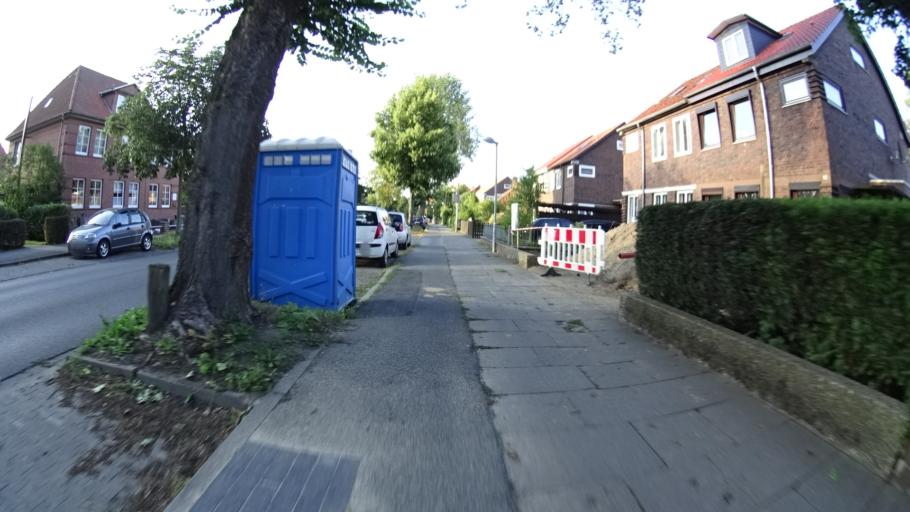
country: DE
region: Lower Saxony
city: Lueneburg
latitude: 53.2379
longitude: 10.3993
